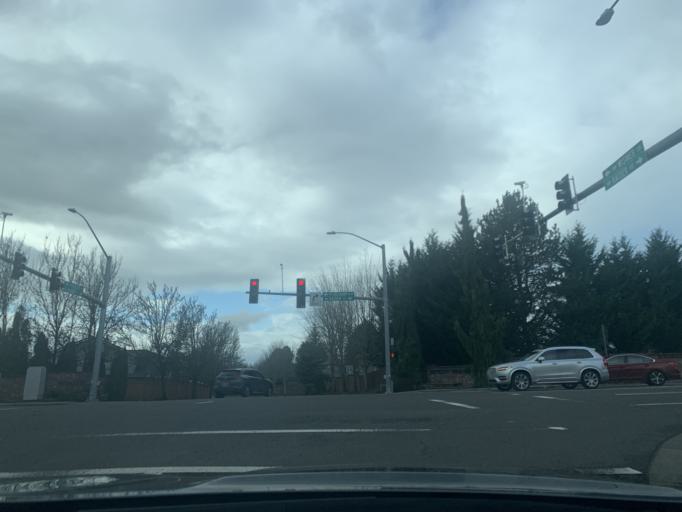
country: US
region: Oregon
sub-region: Washington County
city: Oak Hills
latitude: 45.5599
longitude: -122.8341
